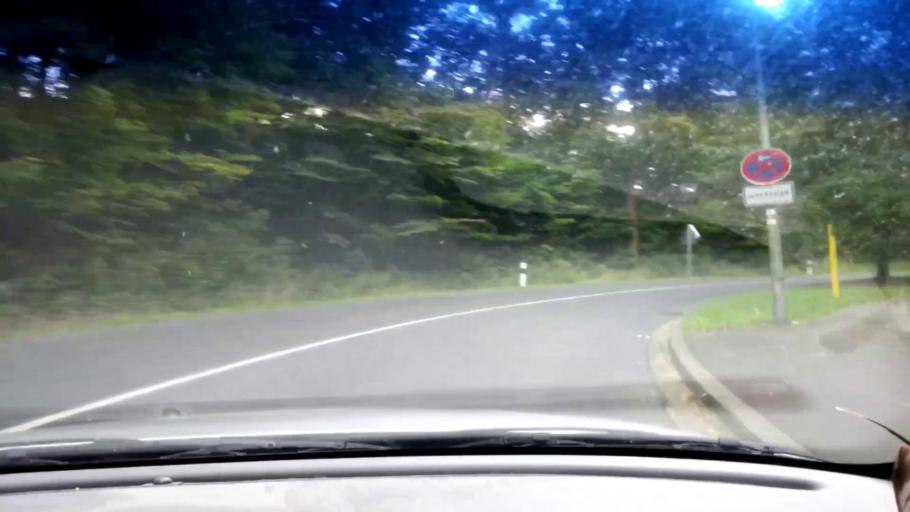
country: DE
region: Bavaria
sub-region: Upper Franconia
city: Schirnding
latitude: 50.0798
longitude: 12.2303
